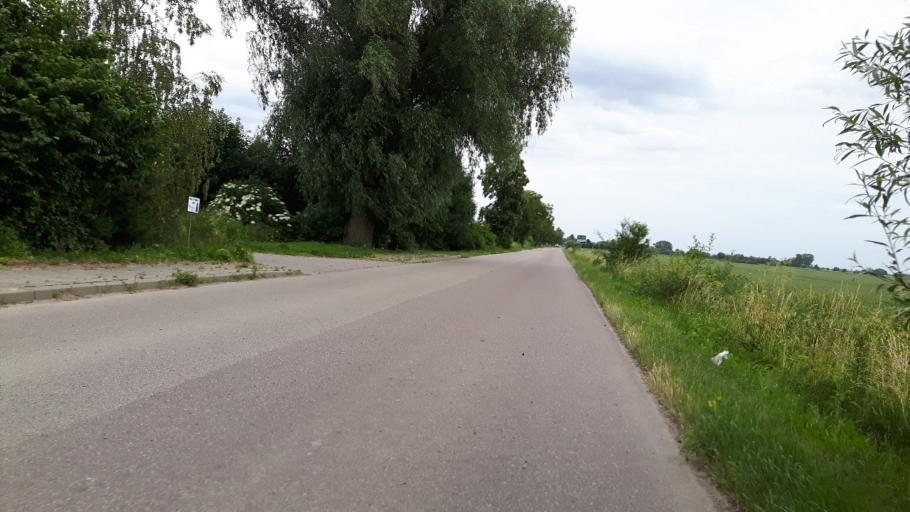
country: PL
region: Warmian-Masurian Voivodeship
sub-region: Powiat elblaski
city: Gronowo Elblaskie
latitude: 54.2118
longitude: 19.2656
